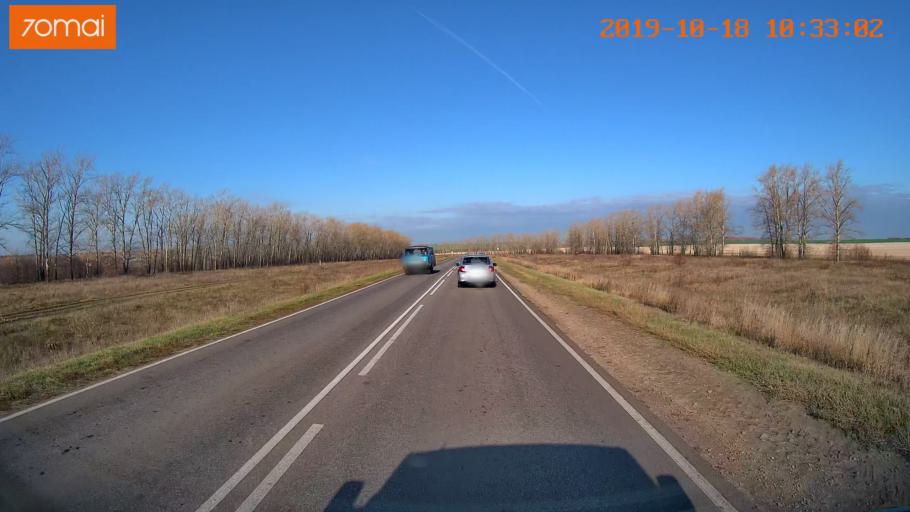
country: RU
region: Tula
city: Kurkino
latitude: 53.5028
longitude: 38.6180
